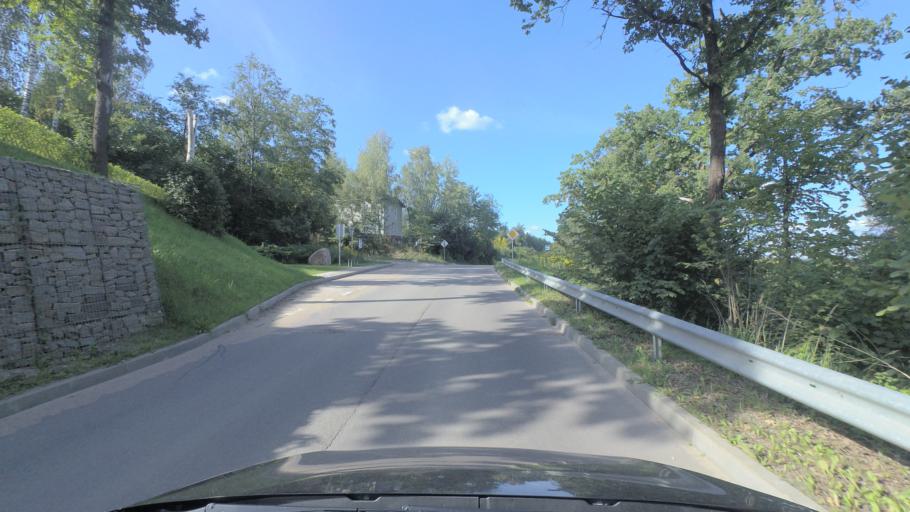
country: LT
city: Nemencine
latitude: 54.8496
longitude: 25.3737
